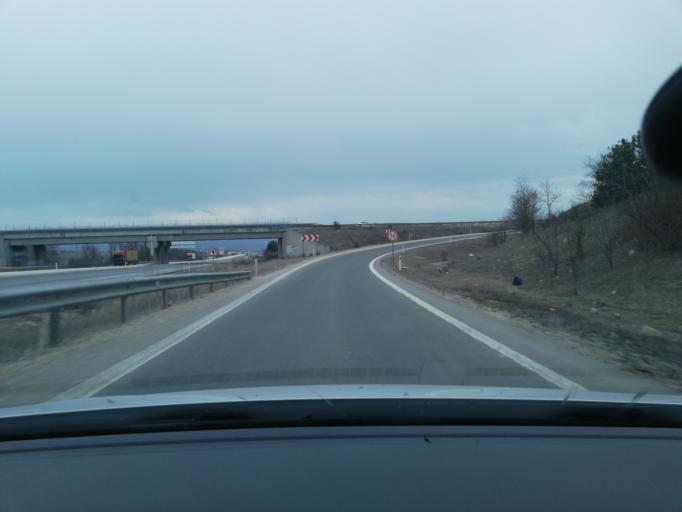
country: TR
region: Bolu
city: Gerede
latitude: 40.7776
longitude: 32.2171
